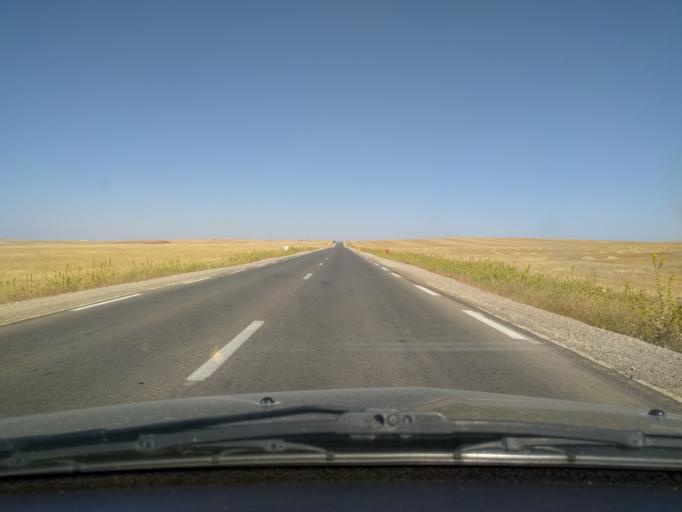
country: DZ
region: Tiaret
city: Frenda
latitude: 34.8815
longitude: 1.1935
